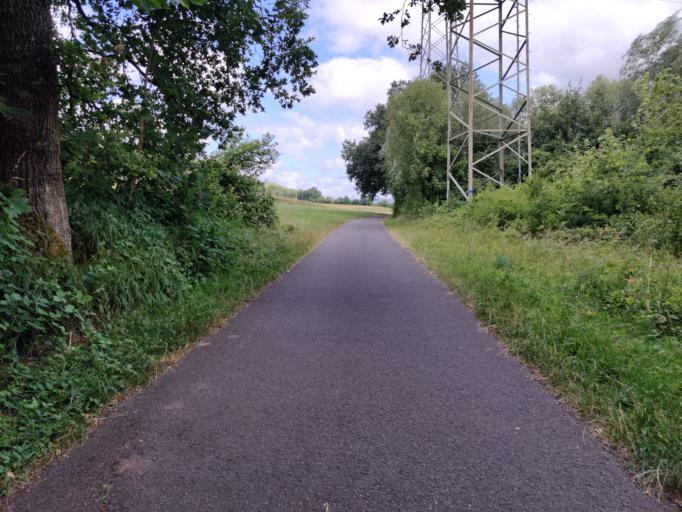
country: DE
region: Rheinland-Pfalz
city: Roxheim
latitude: 49.8715
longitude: 7.8092
